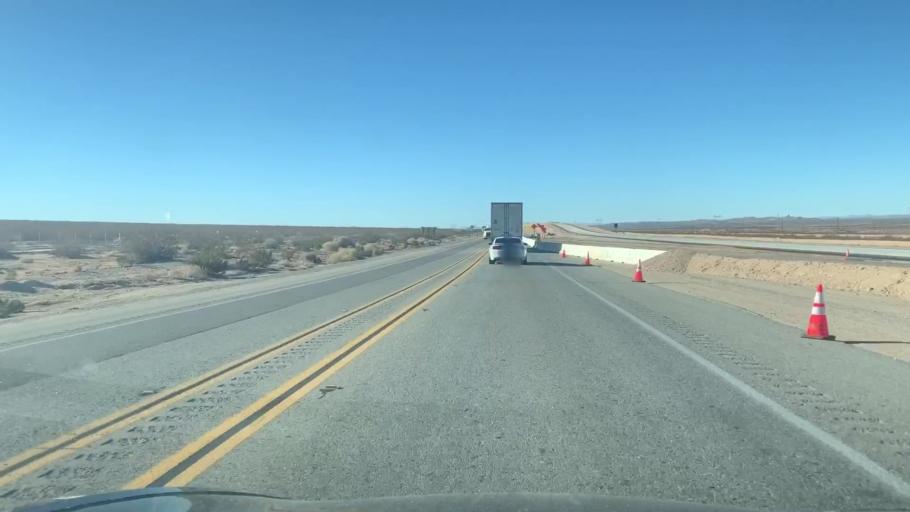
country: US
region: California
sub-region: Kern County
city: Boron
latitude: 34.9839
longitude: -117.4853
